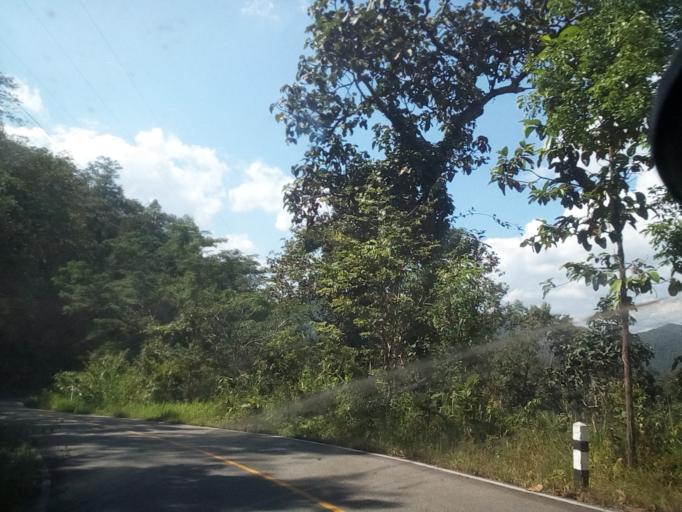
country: TH
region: Chiang Mai
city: Samoeng
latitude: 18.8766
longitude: 98.6889
